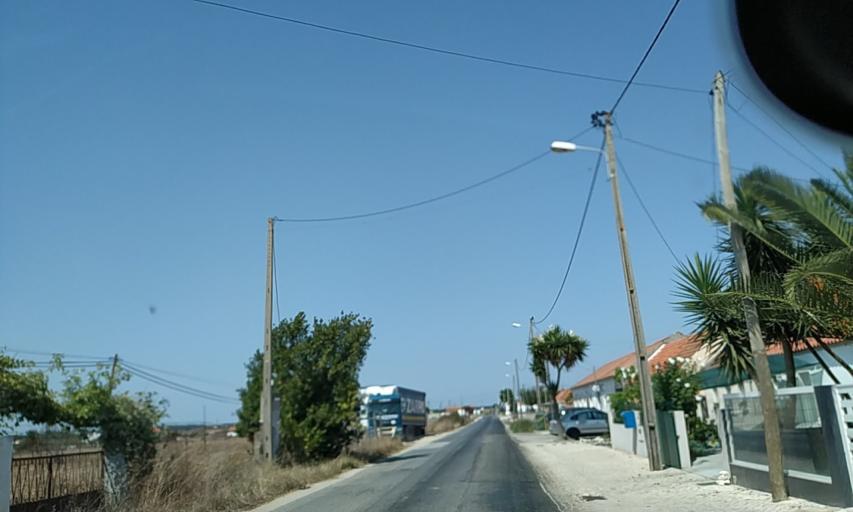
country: PT
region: Santarem
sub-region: Benavente
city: Poceirao
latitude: 38.6982
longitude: -8.7251
